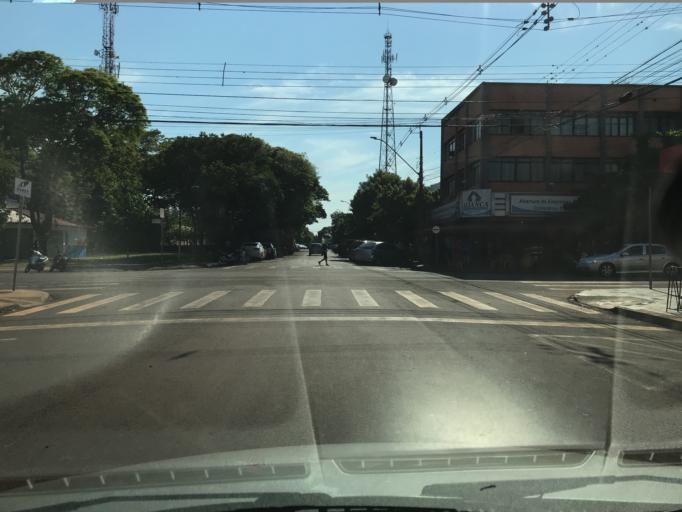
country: BR
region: Parana
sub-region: Palotina
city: Palotina
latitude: -24.2819
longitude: -53.8394
